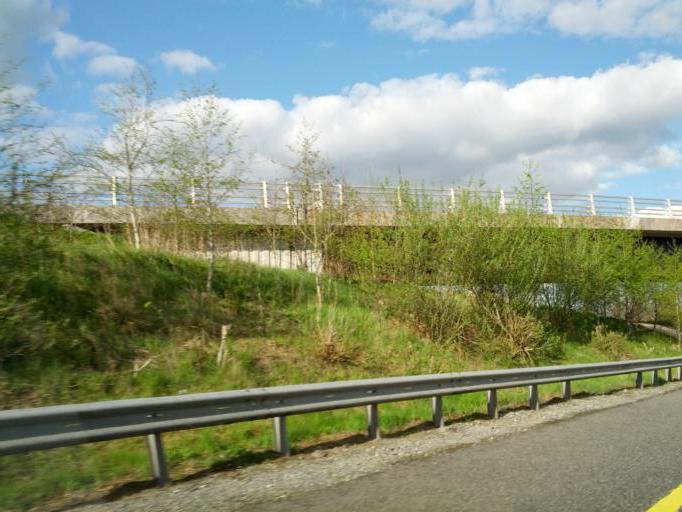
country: IE
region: Leinster
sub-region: An Iarmhi
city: Rathwire
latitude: 53.4489
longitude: -7.1717
